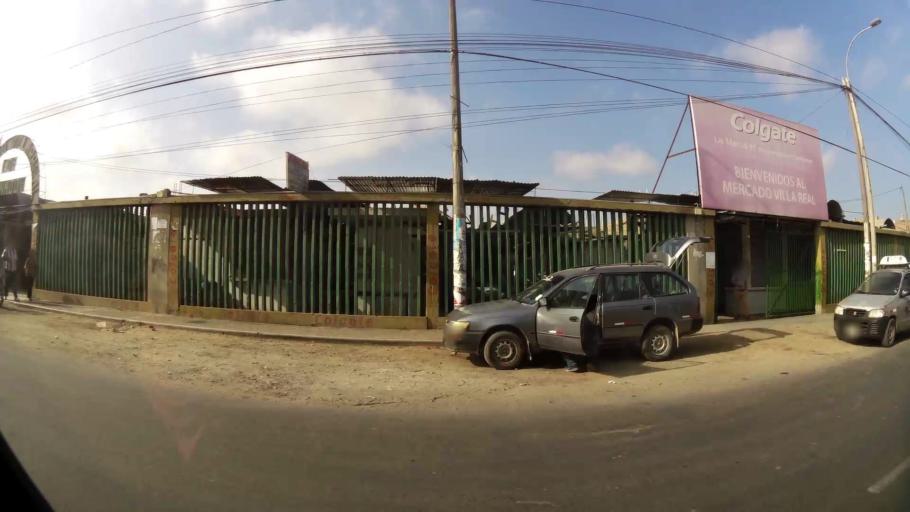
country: PE
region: La Libertad
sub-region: Provincia de Trujillo
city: El Porvenir
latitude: -8.0947
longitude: -79.0141
